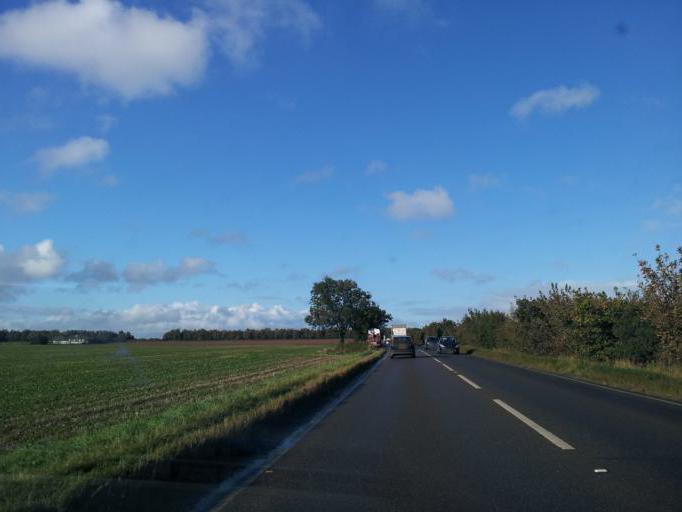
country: GB
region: England
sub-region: Norfolk
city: King's Lynn
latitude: 52.7159
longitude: 0.4876
